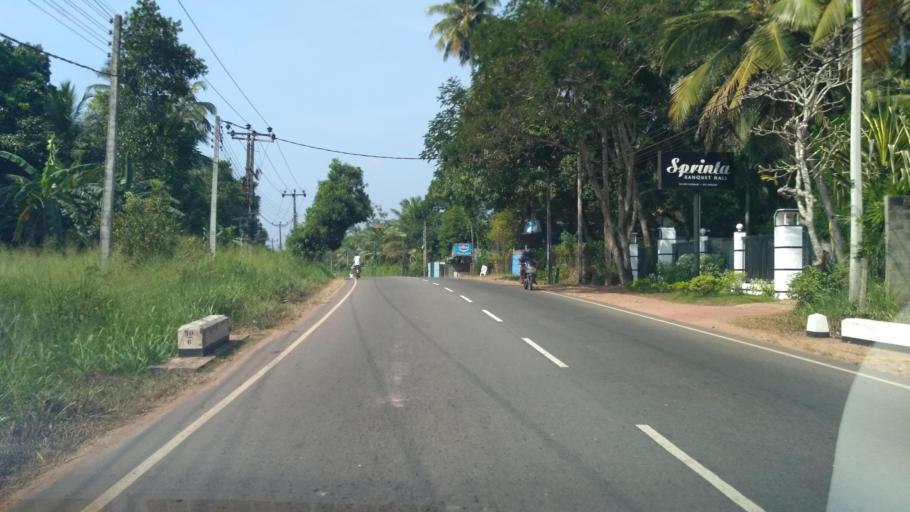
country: LK
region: North Western
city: Kuliyapitiya
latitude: 7.3326
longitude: 80.0016
